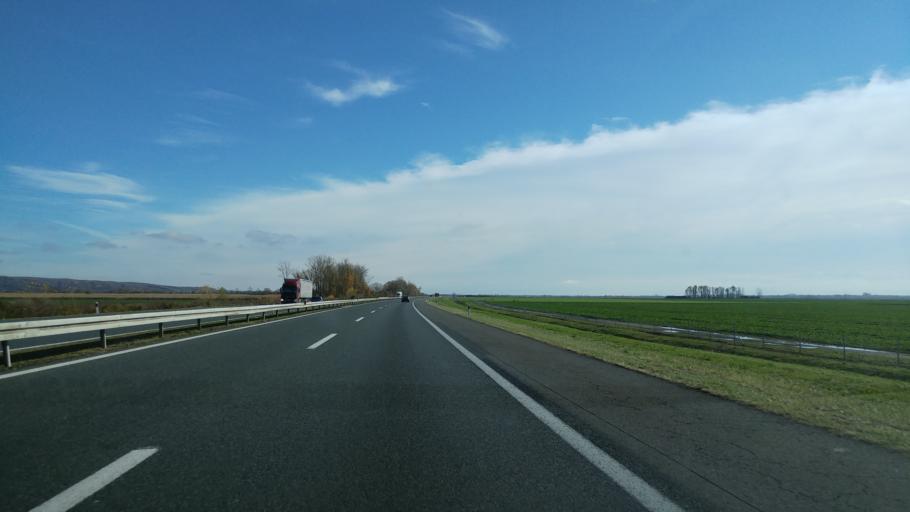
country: HR
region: Brodsko-Posavska
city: Okucani
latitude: 45.2869
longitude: 17.1033
